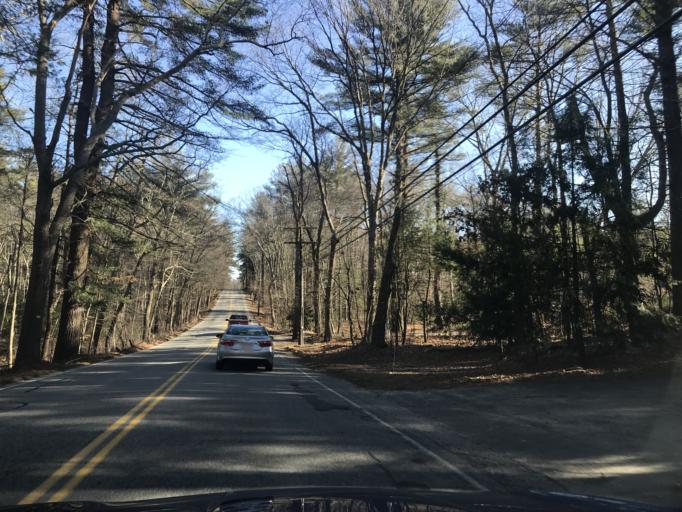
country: US
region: Massachusetts
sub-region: Essex County
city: Groveland
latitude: 42.7119
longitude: -71.0376
